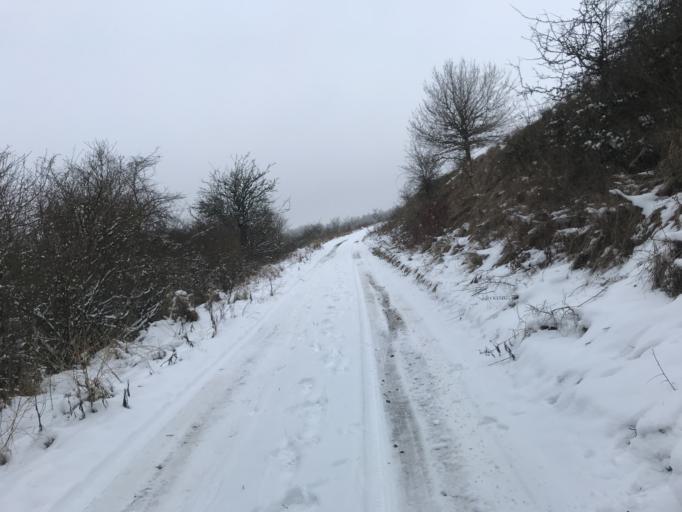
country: FR
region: Lorraine
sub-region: Departement de la Moselle
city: Russange
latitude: 49.4821
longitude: 5.9461
